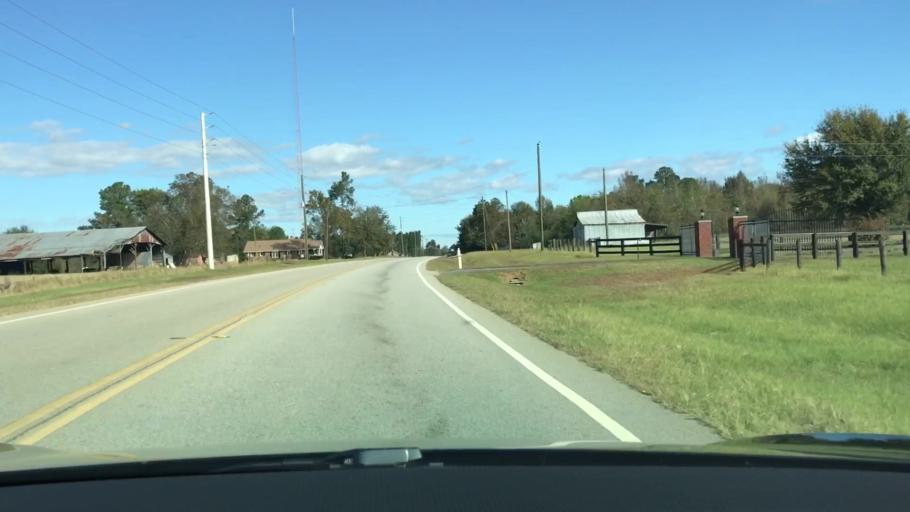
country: US
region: Georgia
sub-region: Jefferson County
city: Wrens
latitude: 33.1609
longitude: -82.4567
